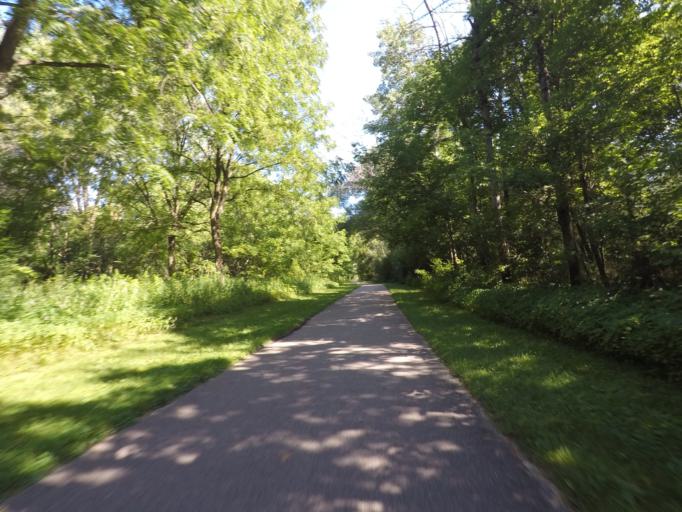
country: US
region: Wisconsin
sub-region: Waukesha County
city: Elm Grove
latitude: 43.0330
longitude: -88.0681
